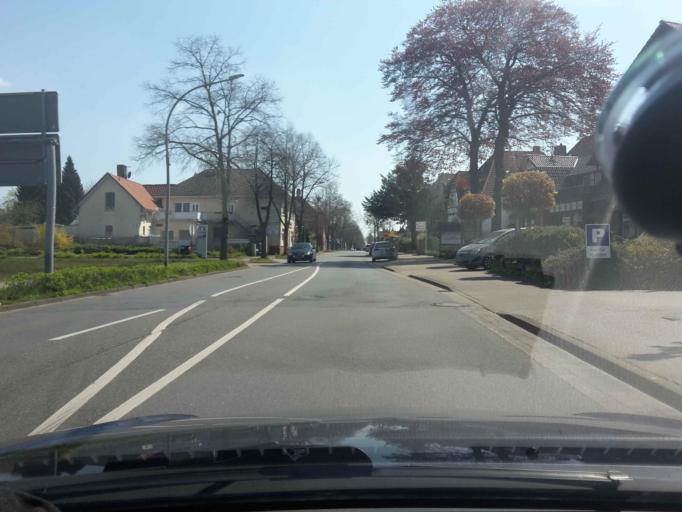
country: DE
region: Lower Saxony
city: Schneverdingen
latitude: 53.1152
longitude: 9.7890
